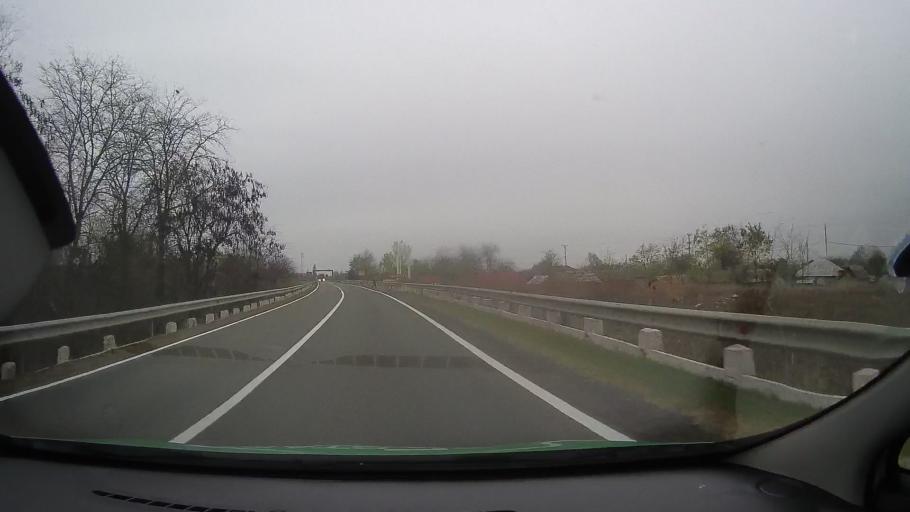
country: RO
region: Ialomita
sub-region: Comuna Giurgeni
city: Giurgeni
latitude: 44.7528
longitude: 27.8576
